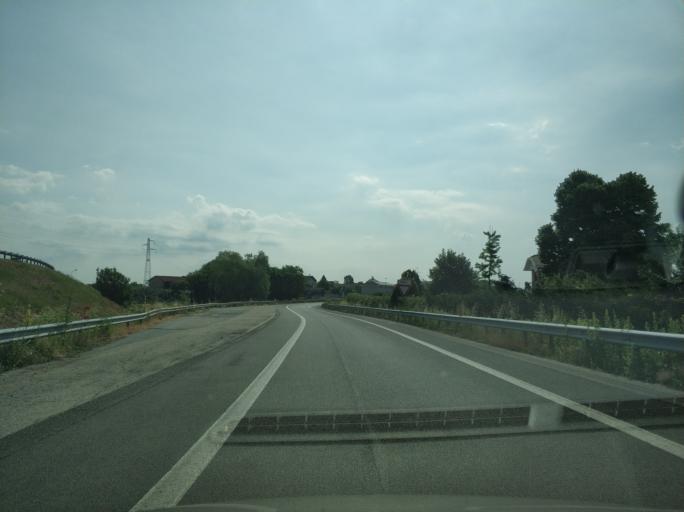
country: IT
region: Piedmont
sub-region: Provincia di Torino
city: Cambiano
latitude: 44.9584
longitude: 7.7821
